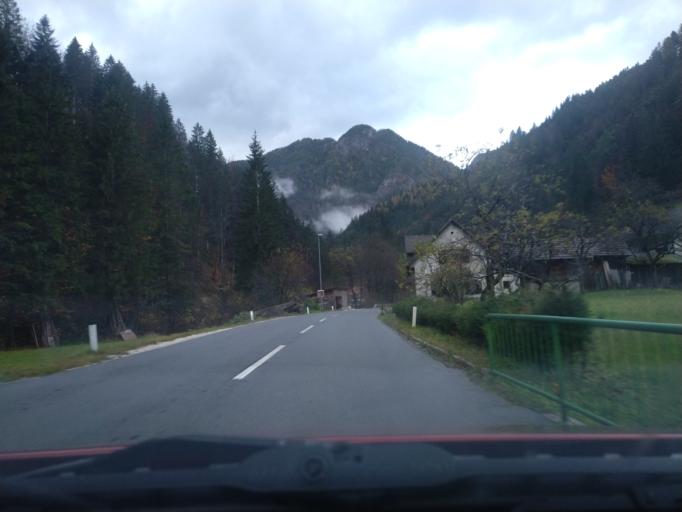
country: SI
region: Solcava
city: Solcava
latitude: 46.4169
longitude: 14.6987
